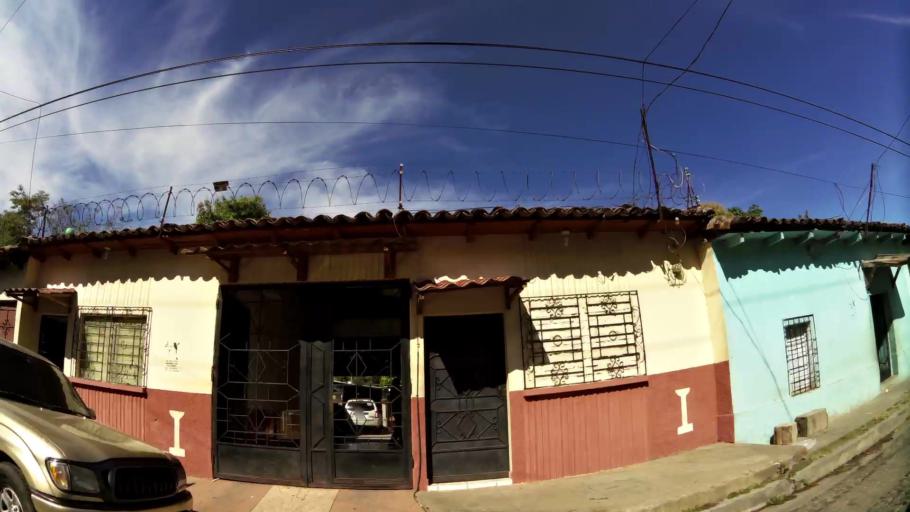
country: SV
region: Cuscatlan
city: Suchitoto
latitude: 13.9310
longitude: -89.0303
